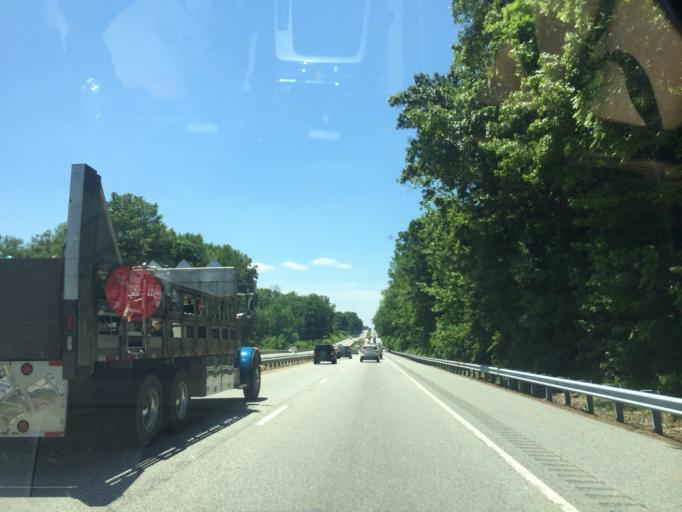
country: US
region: Maryland
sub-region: Talbot County
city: Easton
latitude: 38.8900
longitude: -76.0616
